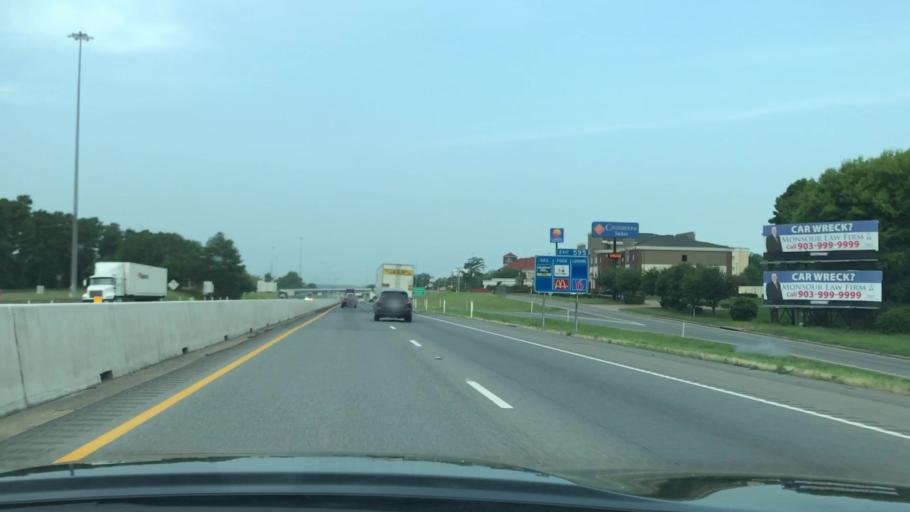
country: US
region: Texas
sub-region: Gregg County
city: Longview
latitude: 32.4495
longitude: -94.7108
